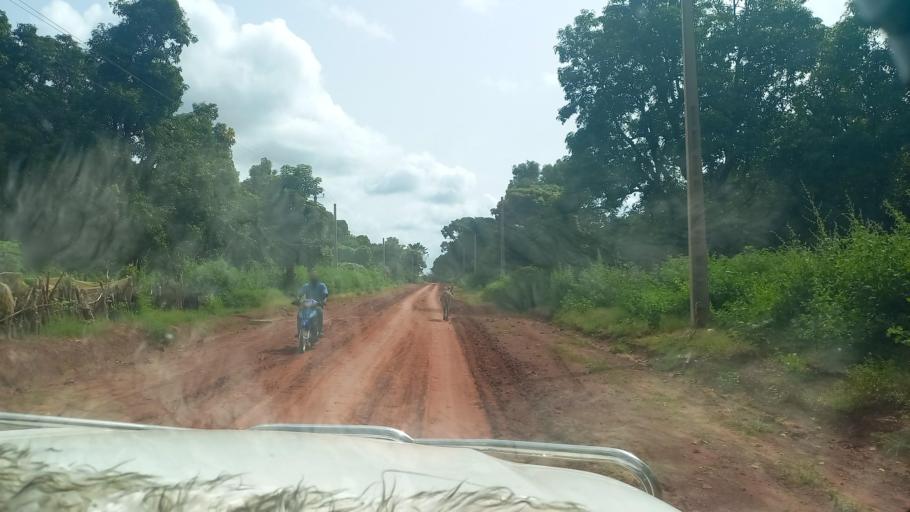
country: SN
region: Ziguinchor
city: Bignona
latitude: 12.7564
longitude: -16.2689
